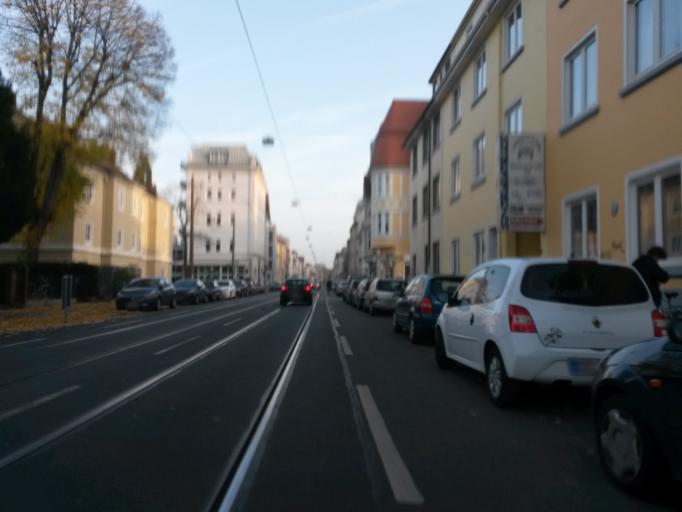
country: DE
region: Bremen
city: Bremen
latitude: 53.0659
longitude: 8.8050
